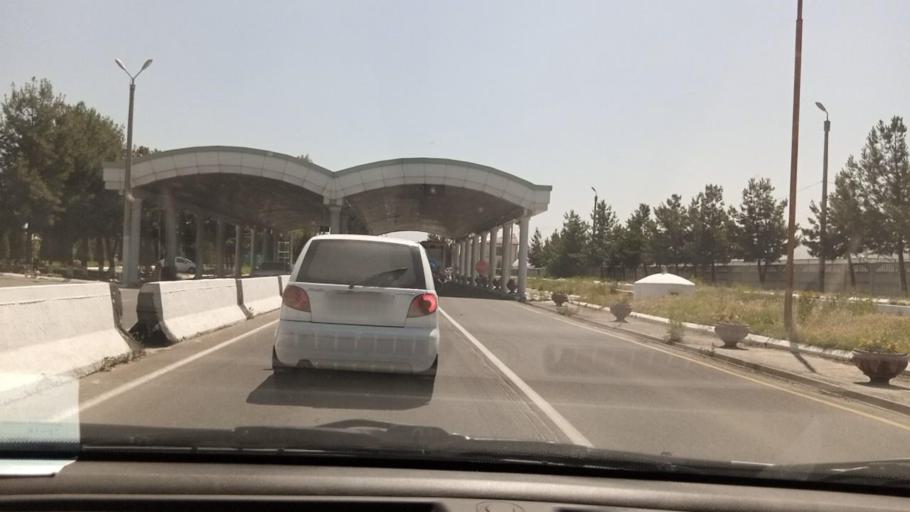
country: UZ
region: Toshkent
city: Urtaowul
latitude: 41.2155
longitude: 69.1731
